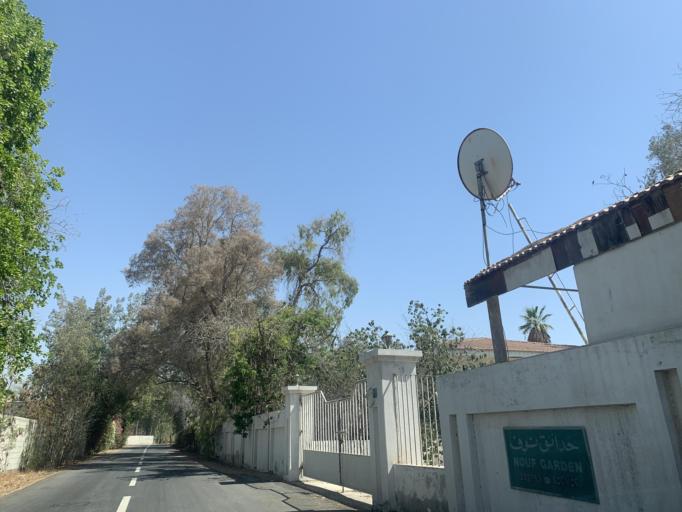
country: BH
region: Manama
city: Jidd Hafs
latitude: 26.2266
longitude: 50.5022
